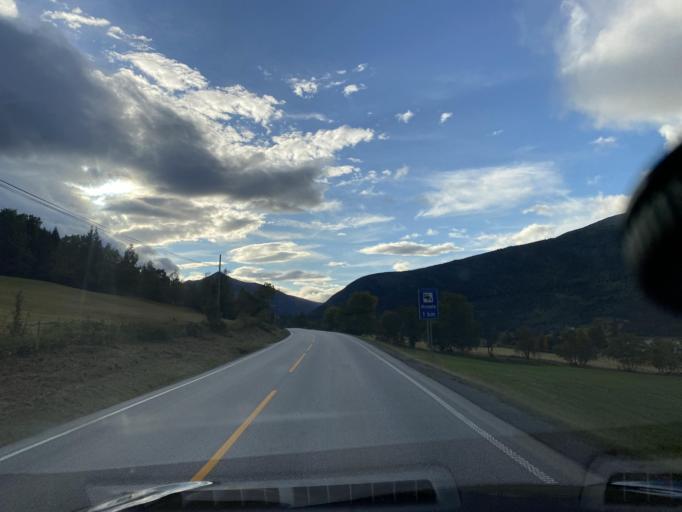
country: NO
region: Oppland
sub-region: Lom
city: Fossbergom
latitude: 61.8535
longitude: 8.6549
